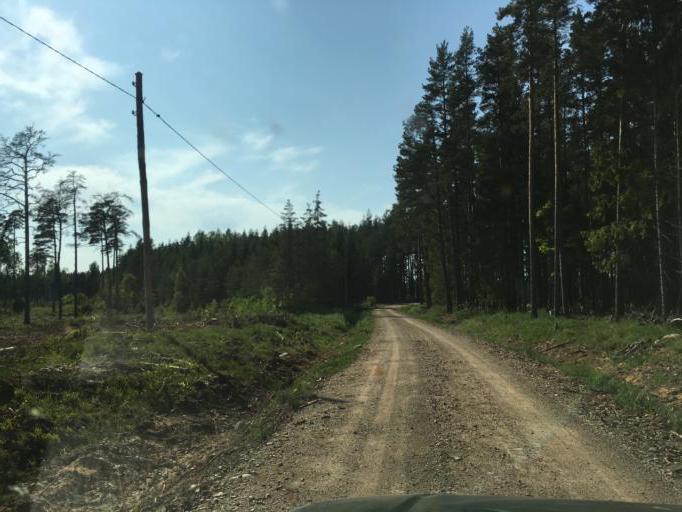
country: LV
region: Dundaga
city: Dundaga
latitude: 57.6119
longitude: 22.5061
